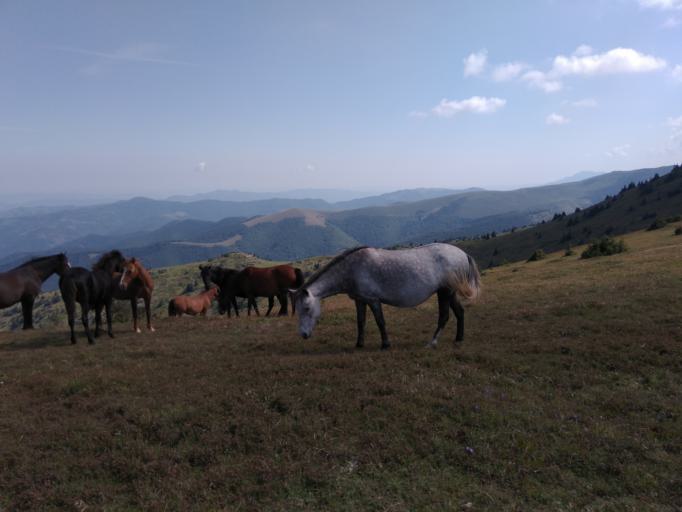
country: BG
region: Plovdiv
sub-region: Obshtina Karlovo
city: Karlovo
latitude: 42.7314
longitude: 24.7362
